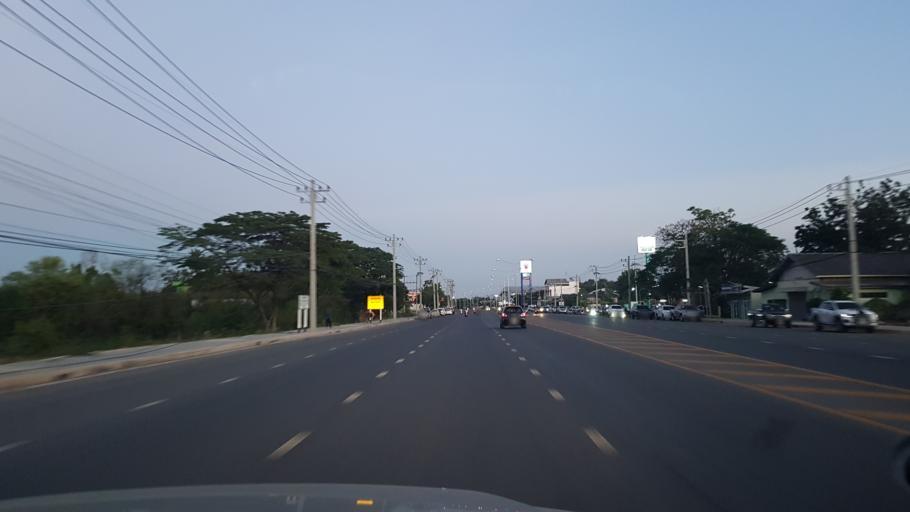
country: TH
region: Chaiyaphum
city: Phu Khiao
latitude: 16.3649
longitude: 102.1394
